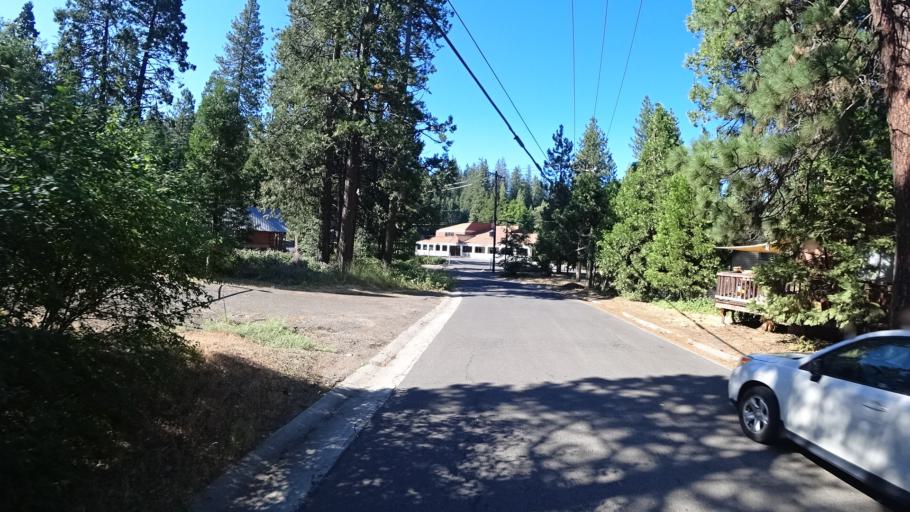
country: US
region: California
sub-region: Calaveras County
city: Arnold
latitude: 38.2563
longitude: -120.3517
